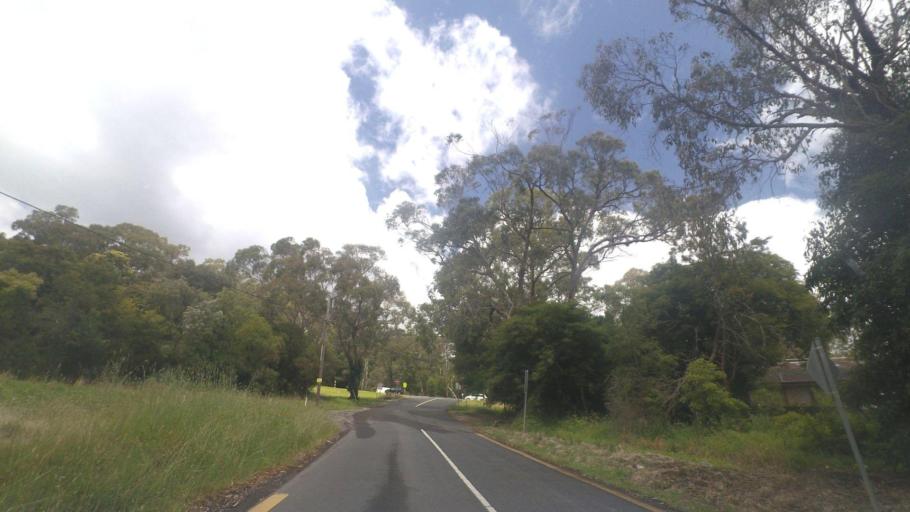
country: AU
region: Victoria
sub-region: Yarra Ranges
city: Mount Evelyn
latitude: -37.7805
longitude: 145.3679
